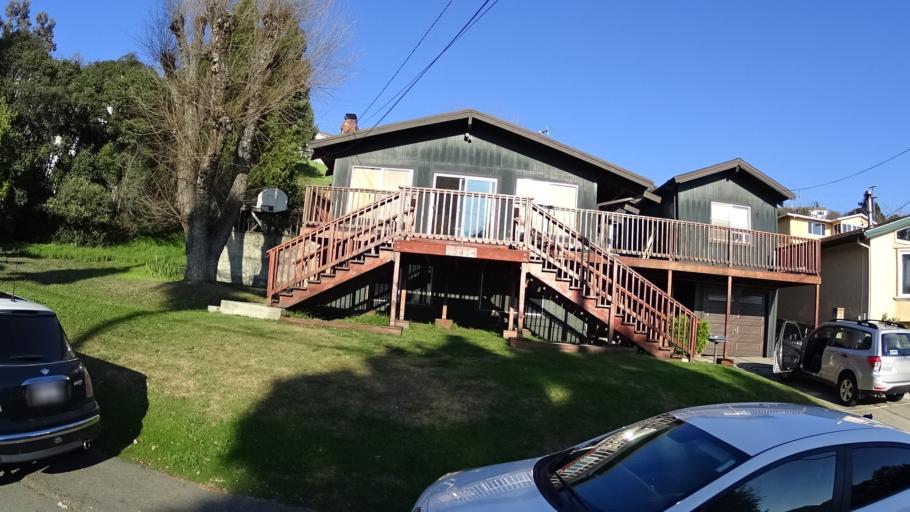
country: US
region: California
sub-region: Alameda County
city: Hayward
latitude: 37.6550
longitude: -122.0652
